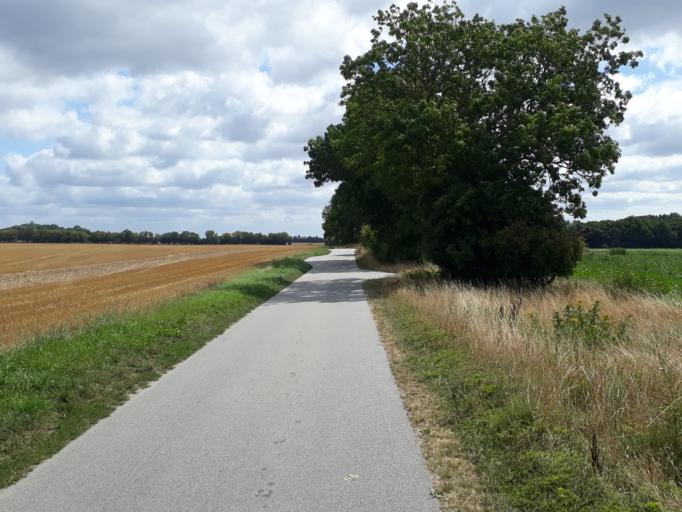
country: DE
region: Mecklenburg-Vorpommern
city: Marlow
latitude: 54.2183
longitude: 12.5601
